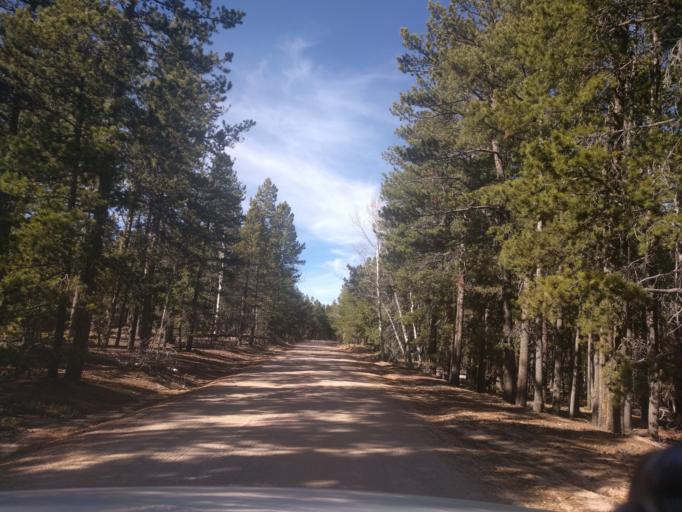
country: US
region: Colorado
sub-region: Douglas County
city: Perry Park
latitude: 39.1907
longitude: -105.0510
